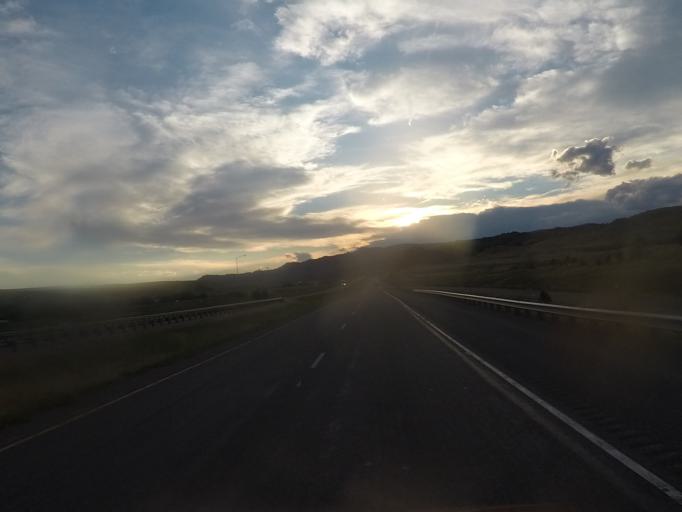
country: US
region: Montana
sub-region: Park County
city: Livingston
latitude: 45.6515
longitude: -110.6124
